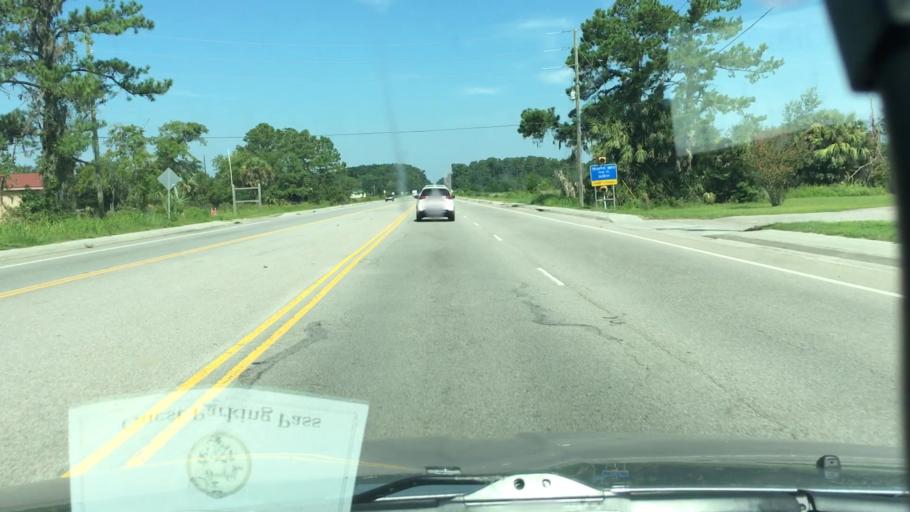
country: US
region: South Carolina
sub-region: Beaufort County
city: Beaufort
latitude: 32.4077
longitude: -80.6379
